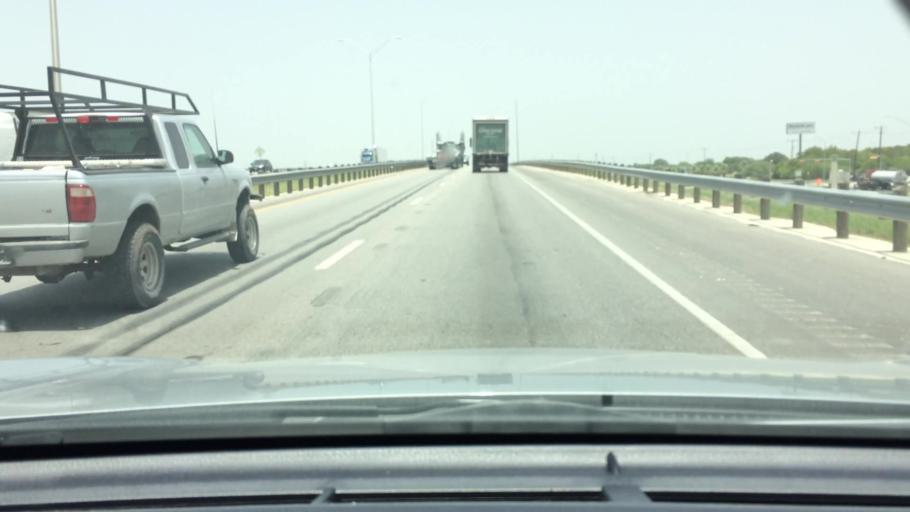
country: US
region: Texas
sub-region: Bexar County
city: Kirby
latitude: 29.4214
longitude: -98.3892
